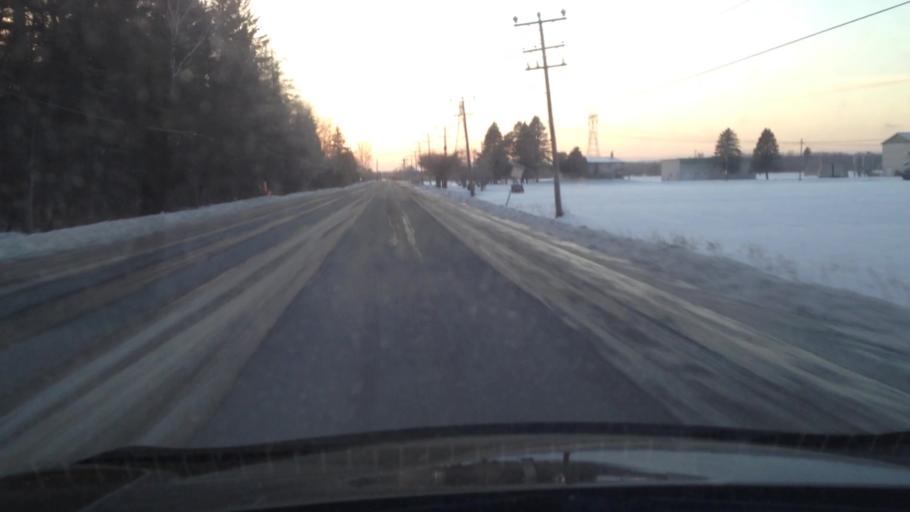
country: CA
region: Quebec
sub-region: Laurentides
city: Sainte-Sophie
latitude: 45.8375
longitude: -73.8342
